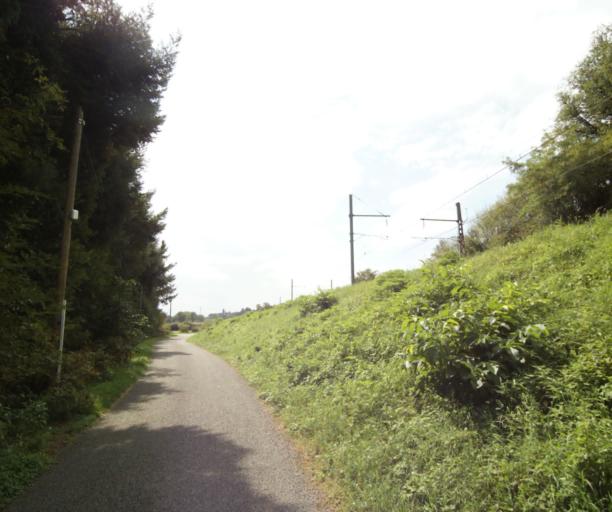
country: FR
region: Bourgogne
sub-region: Departement de Saone-et-Loire
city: Tournus
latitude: 46.5439
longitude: 4.9231
